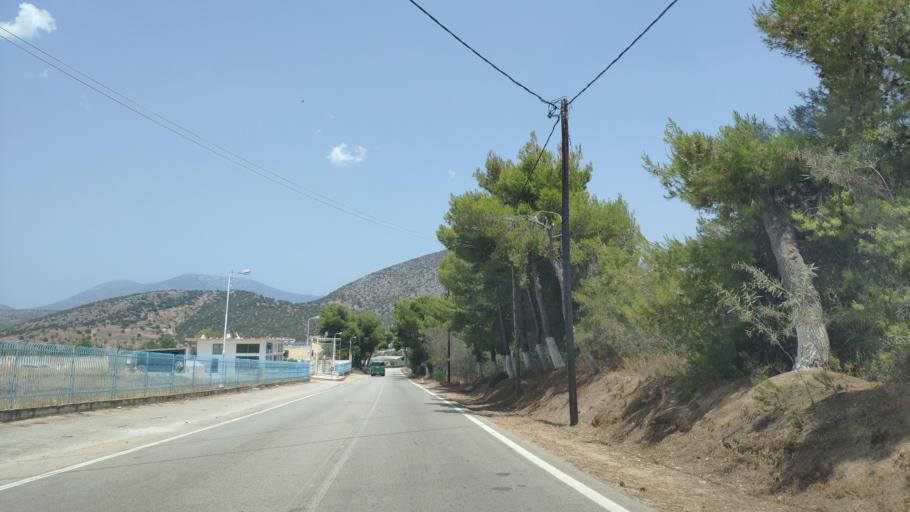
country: GR
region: Peloponnese
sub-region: Nomos Argolidos
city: Kranidi
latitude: 37.3849
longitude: 23.1557
